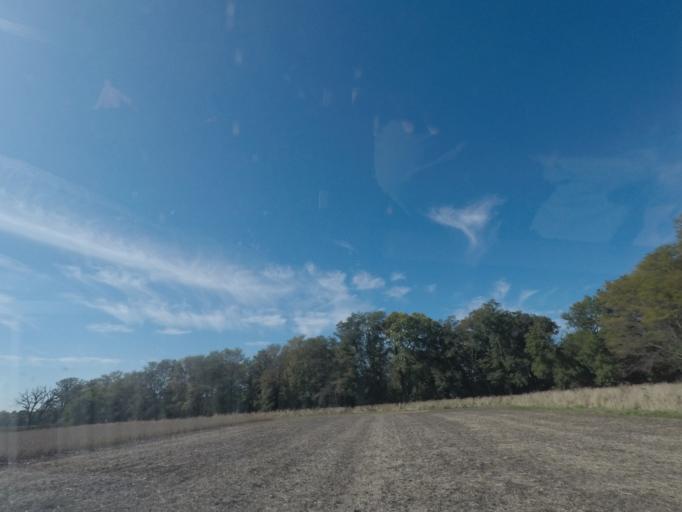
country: US
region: Iowa
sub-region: Story County
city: Nevada
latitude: 42.0312
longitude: -93.3757
